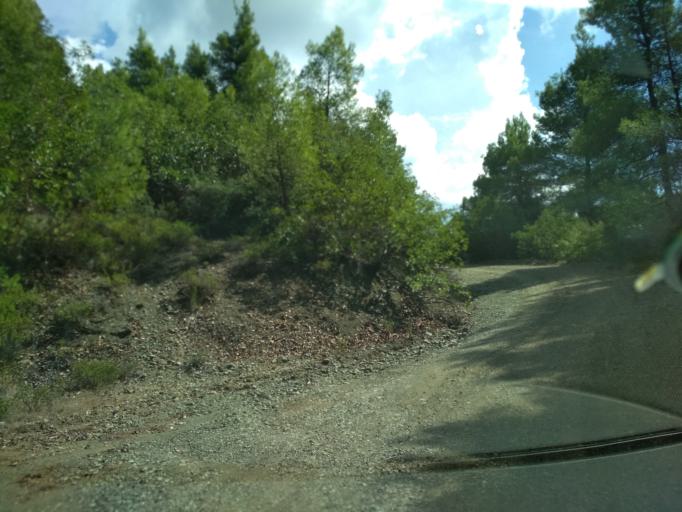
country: GR
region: Central Greece
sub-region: Nomos Evvoias
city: Roviai
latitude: 38.8345
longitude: 23.2763
